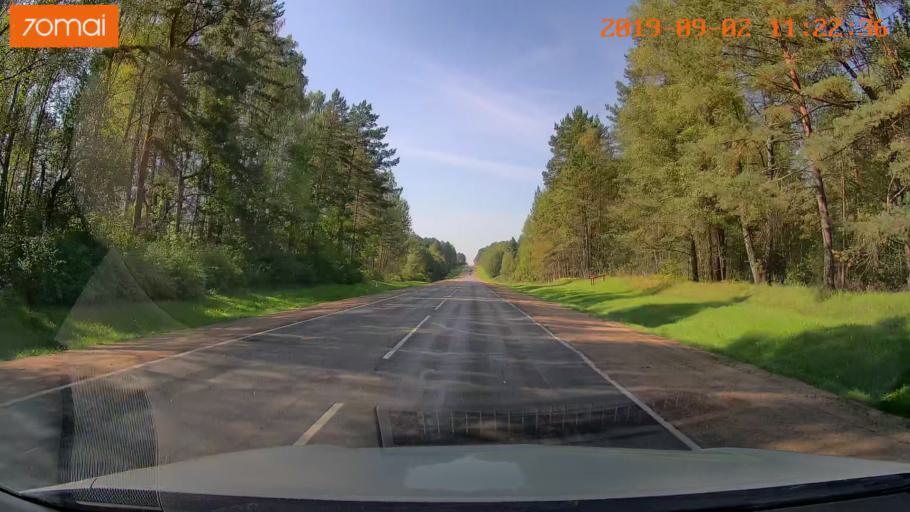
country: RU
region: Smolensk
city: Roslavl'
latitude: 54.0244
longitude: 33.0098
